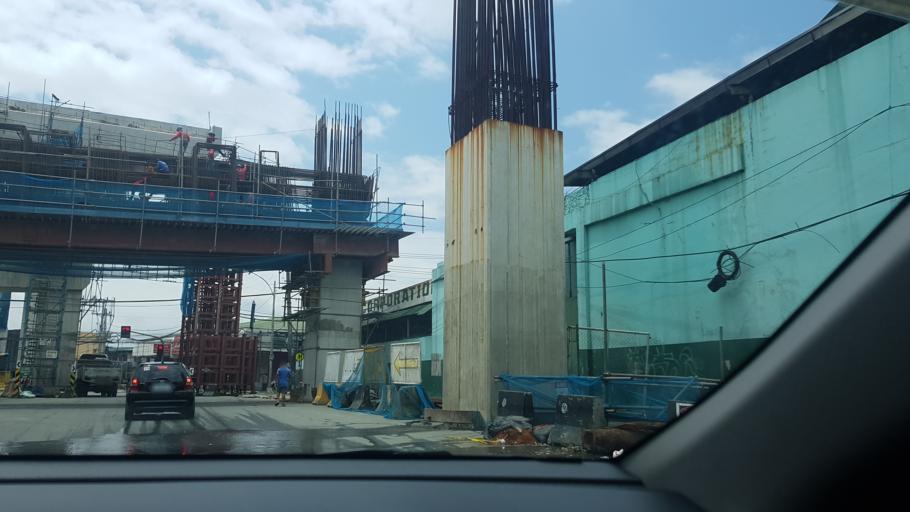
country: PH
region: Calabarzon
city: Del Monte
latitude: 14.6397
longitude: 121.0065
